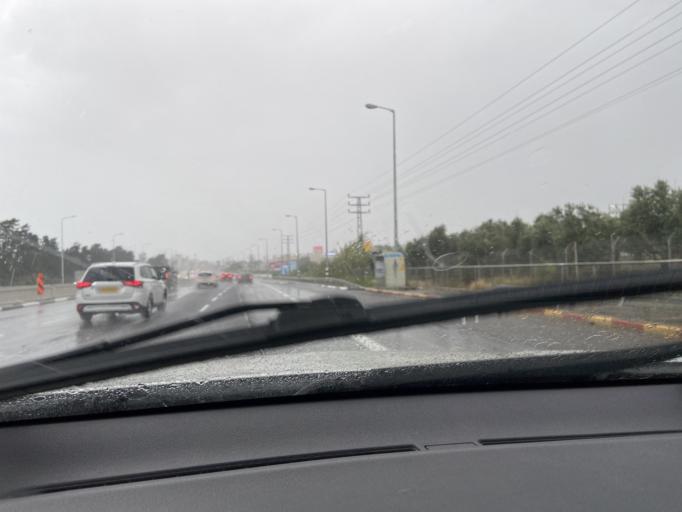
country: IL
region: Northern District
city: El Mazra`a
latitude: 32.9828
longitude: 35.0948
